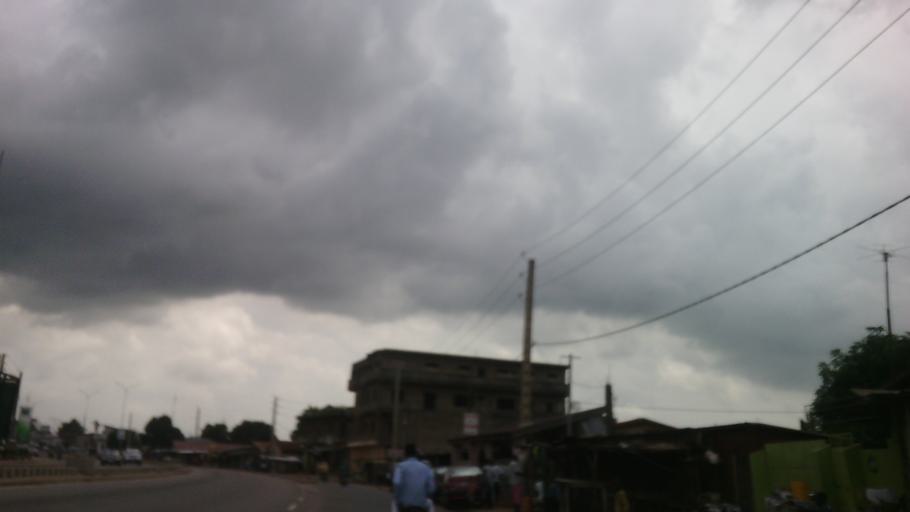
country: BJ
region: Atlantique
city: Abomey-Calavi
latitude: 6.4532
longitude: 2.3573
